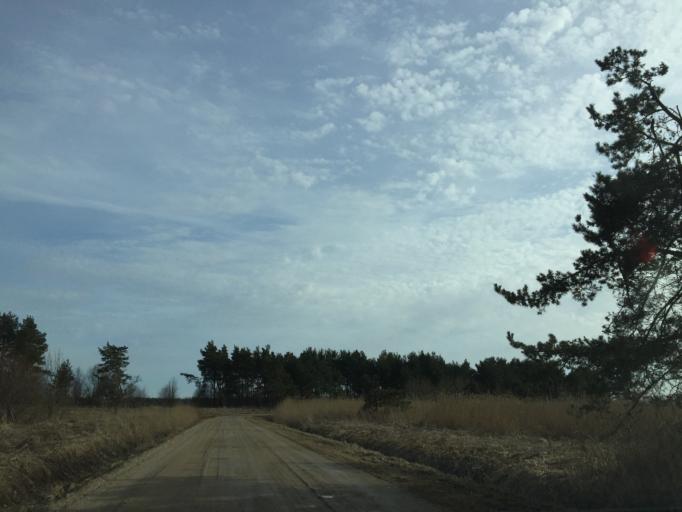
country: EE
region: Paernumaa
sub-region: Paernu linn
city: Parnu
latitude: 58.2390
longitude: 24.4843
